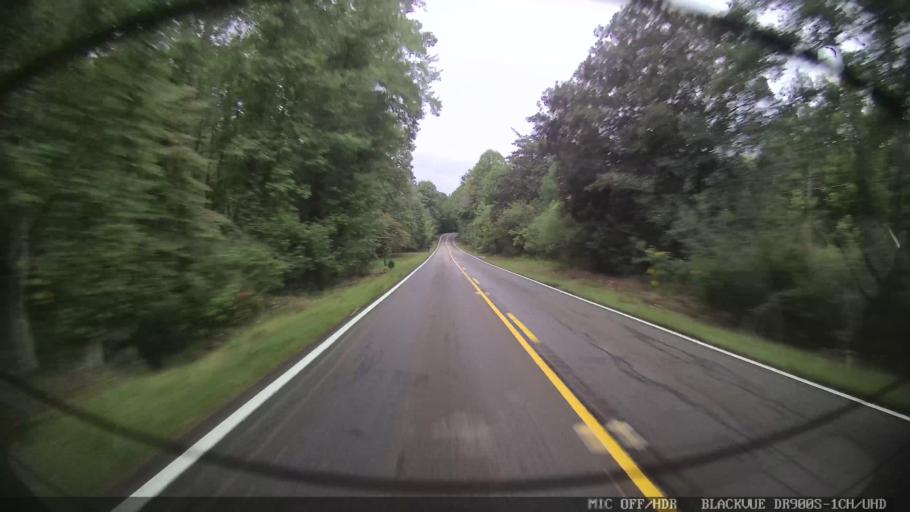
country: US
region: Georgia
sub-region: Gilmer County
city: Ellijay
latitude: 34.7395
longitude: -84.5221
